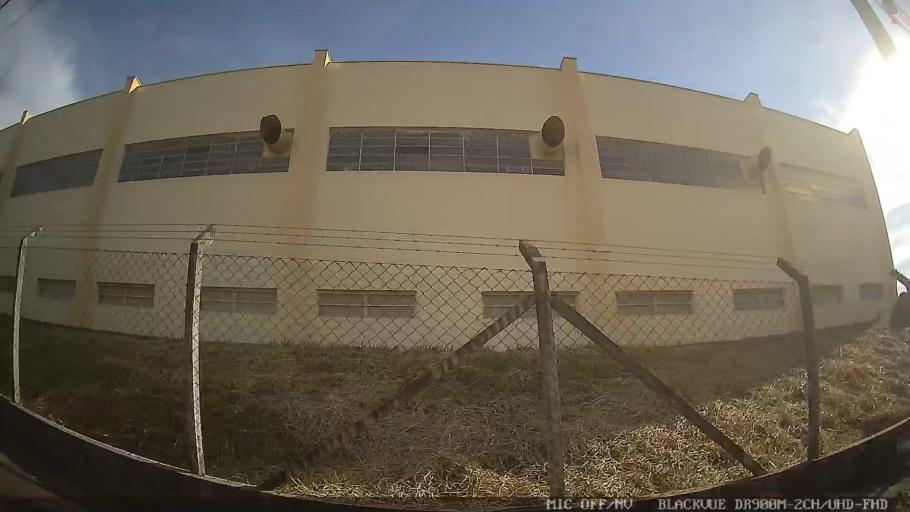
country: BR
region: Sao Paulo
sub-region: Tiete
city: Tiete
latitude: -23.1120
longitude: -47.7129
